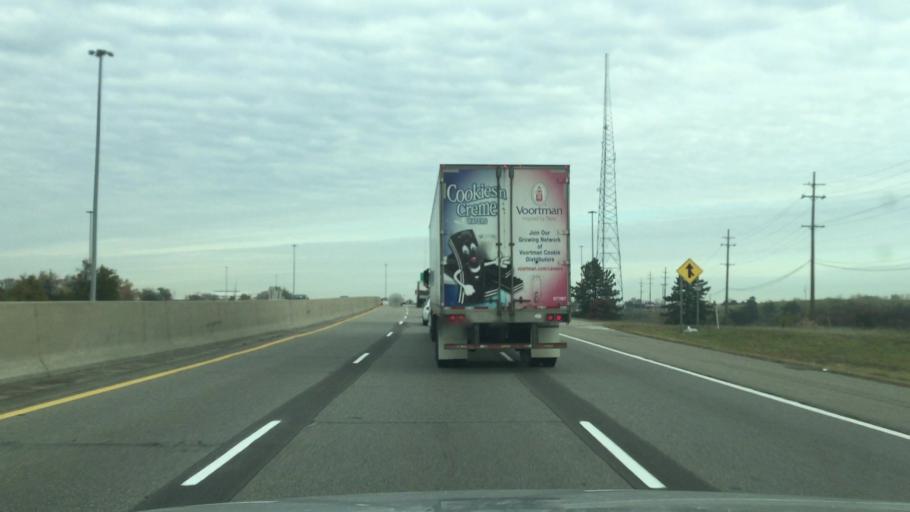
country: US
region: Michigan
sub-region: Oakland County
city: Bingham Farms
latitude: 42.4865
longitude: -83.2847
